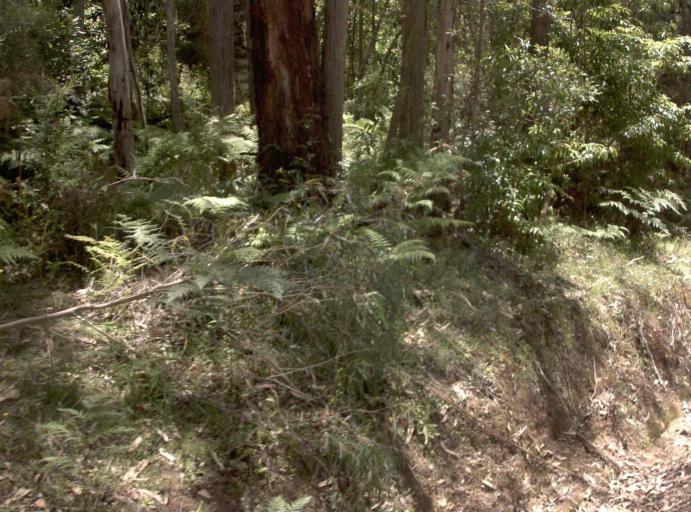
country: AU
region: New South Wales
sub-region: Bombala
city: Bombala
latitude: -37.4882
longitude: 148.9277
